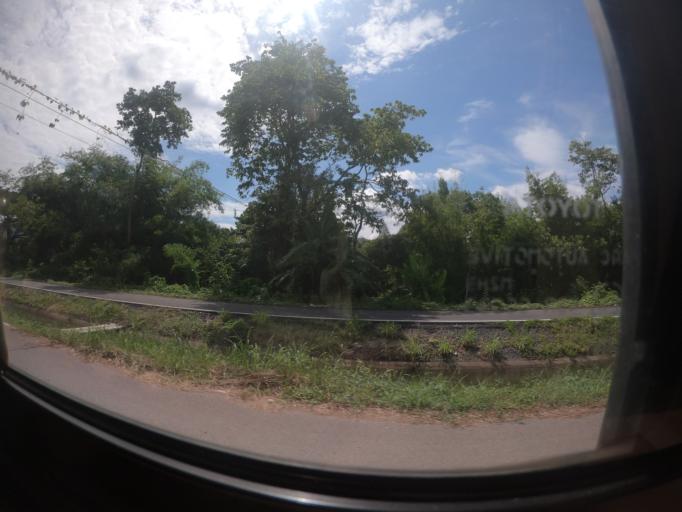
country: TH
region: Nakhon Nayok
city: Nakhon Nayok
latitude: 14.2946
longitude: 101.3052
